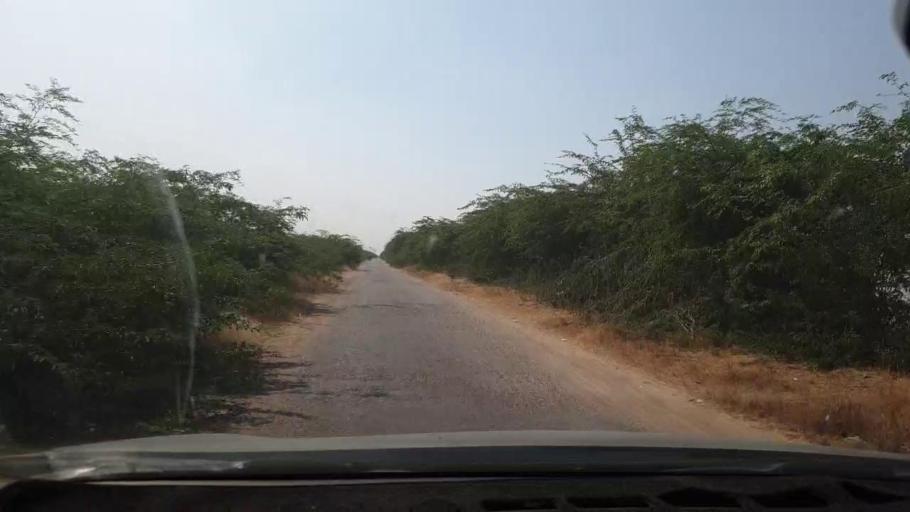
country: PK
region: Sindh
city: Malir Cantonment
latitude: 25.1188
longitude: 67.2145
